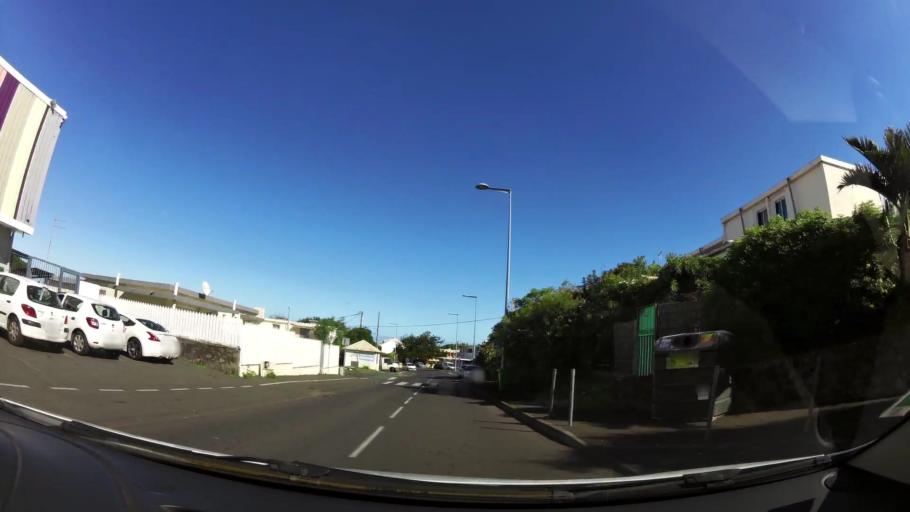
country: RE
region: Reunion
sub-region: Reunion
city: Saint-Pierre
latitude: -21.3427
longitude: 55.4869
